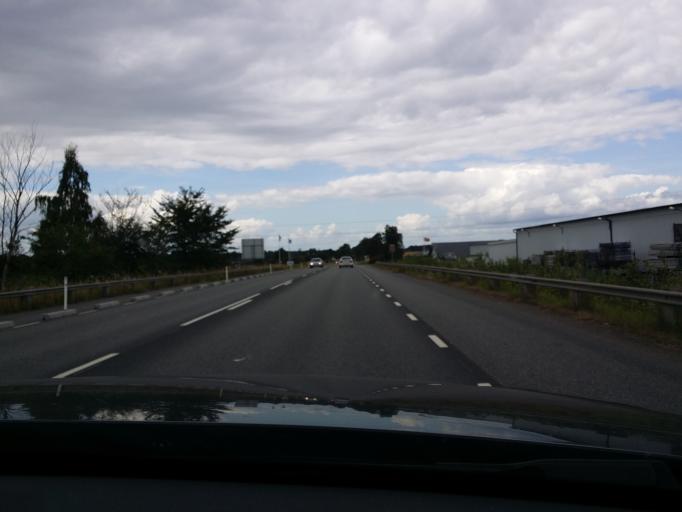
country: SE
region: Skane
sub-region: Bromolla Kommun
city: Bromoella
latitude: 56.0647
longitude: 14.4936
